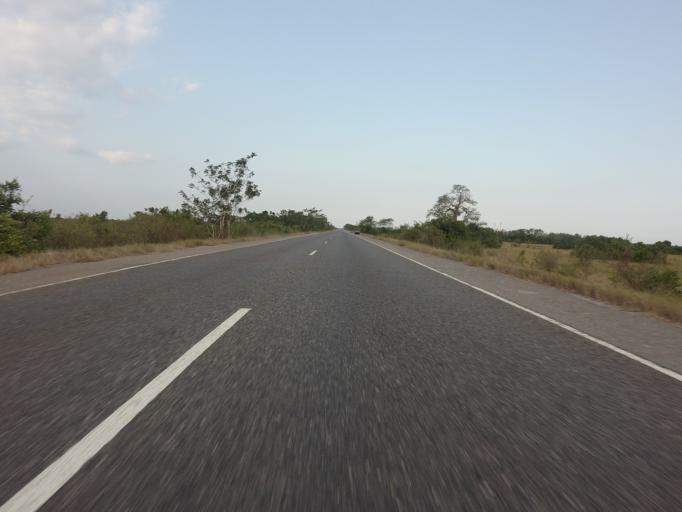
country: GH
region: Volta
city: Anloga
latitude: 6.0820
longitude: 0.5702
